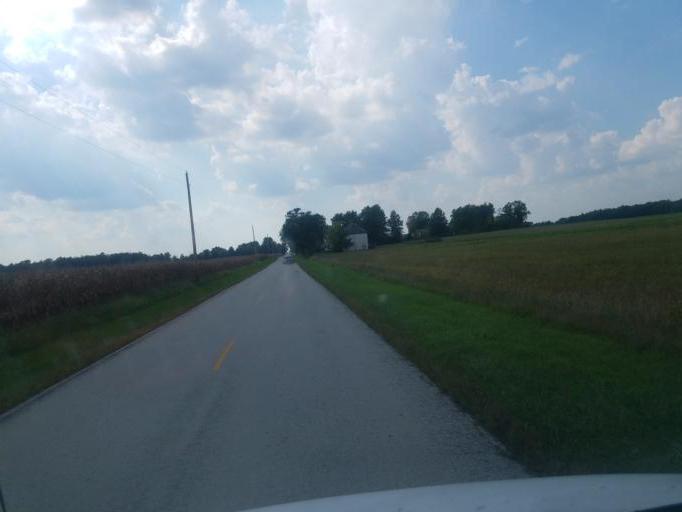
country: US
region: Ohio
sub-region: Hardin County
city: Kenton
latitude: 40.7459
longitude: -83.6083
